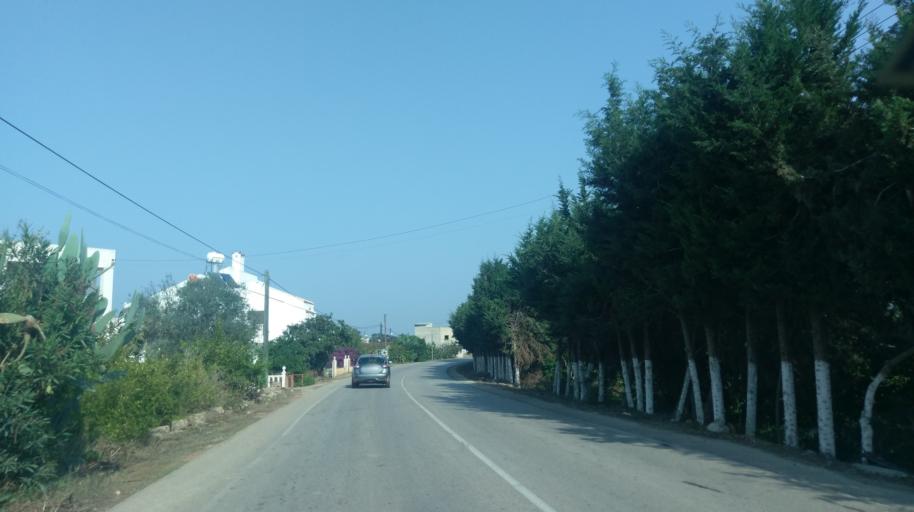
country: CY
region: Ammochostos
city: Leonarisso
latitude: 35.4975
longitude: 34.1586
